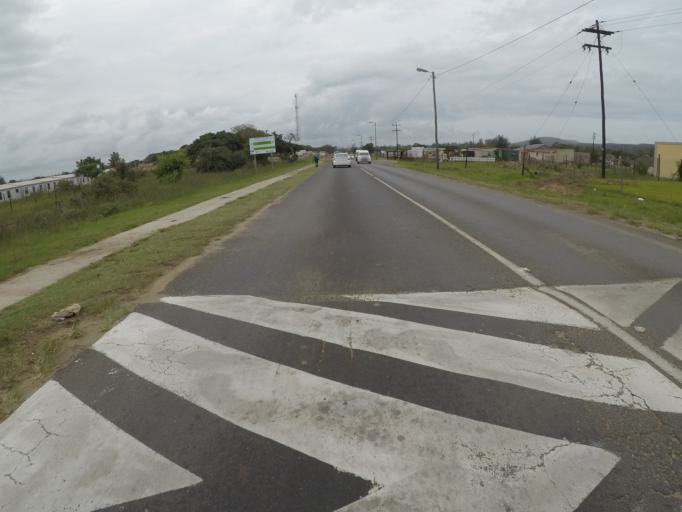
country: ZA
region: KwaZulu-Natal
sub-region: uThungulu District Municipality
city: Richards Bay
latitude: -28.7645
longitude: 32.1314
